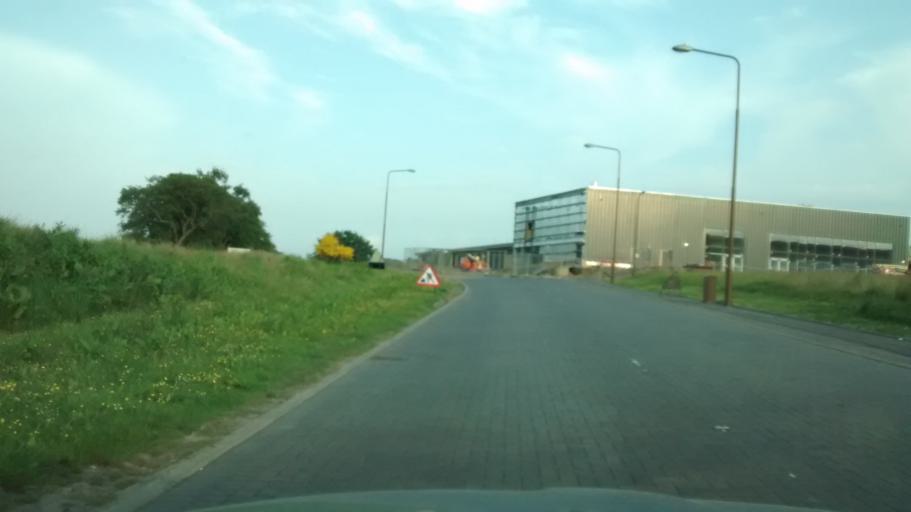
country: GB
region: Scotland
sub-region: West Lothian
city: Armadale
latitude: 55.8873
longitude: -3.6893
